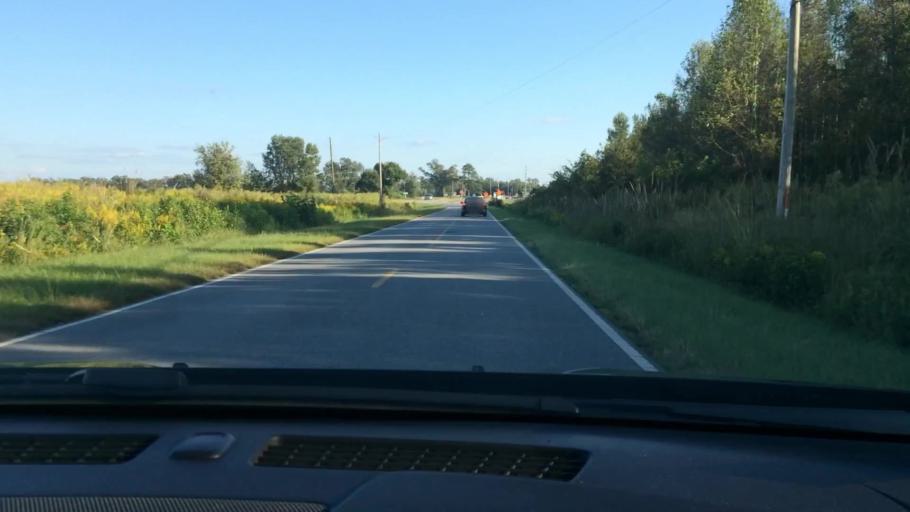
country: US
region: North Carolina
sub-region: Pitt County
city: Ayden
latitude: 35.4934
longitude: -77.4303
